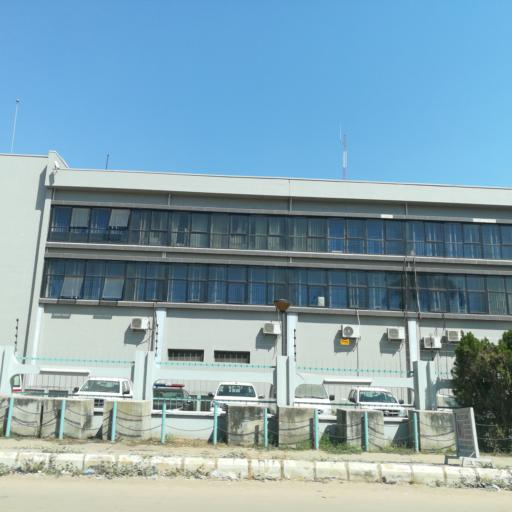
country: NG
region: Kano
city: Kano
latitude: 12.0059
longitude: 8.5412
